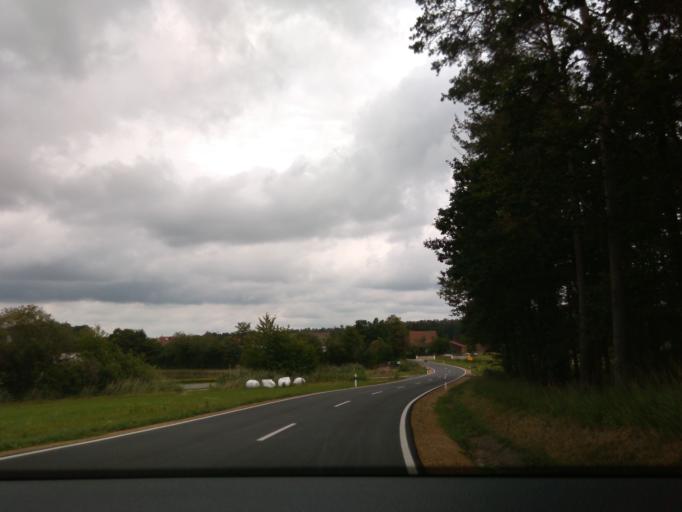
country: DE
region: Bavaria
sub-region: Regierungsbezirk Mittelfranken
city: Gremsdorf
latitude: 49.6741
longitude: 10.8075
